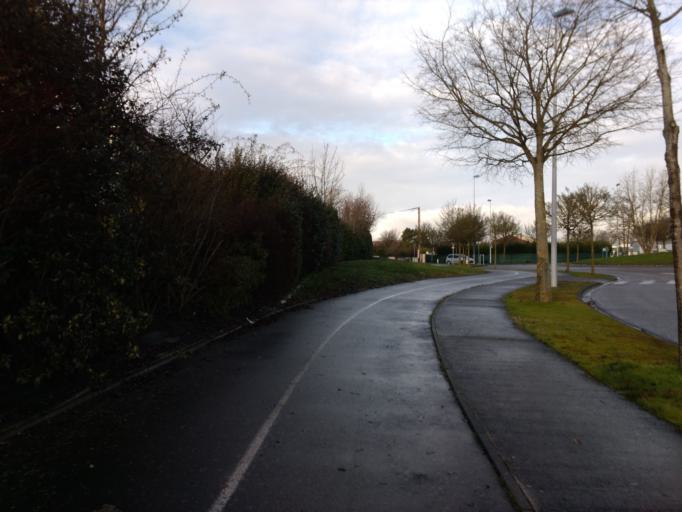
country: FR
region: Midi-Pyrenees
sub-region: Departement de la Haute-Garonne
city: Tournefeuille
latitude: 43.6022
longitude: 1.3196
